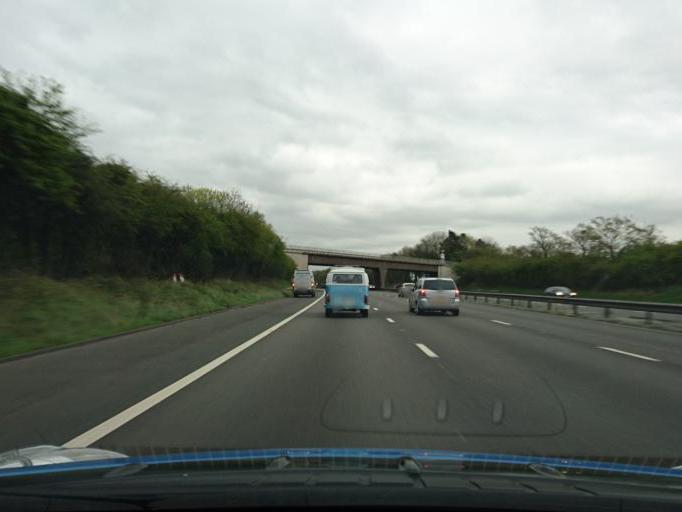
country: GB
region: England
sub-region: Staffordshire
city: Stafford
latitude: 52.7897
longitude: -2.1438
